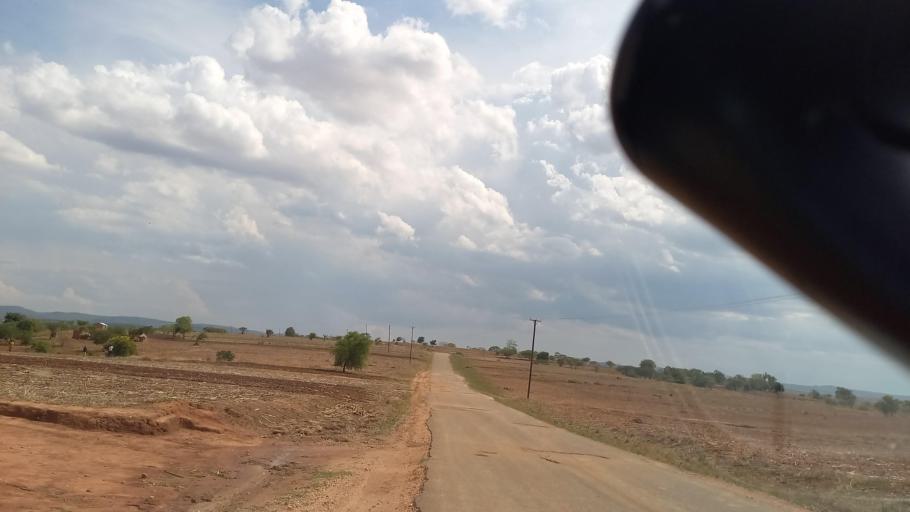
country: ZM
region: Lusaka
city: Kafue
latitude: -16.1808
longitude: 28.0881
